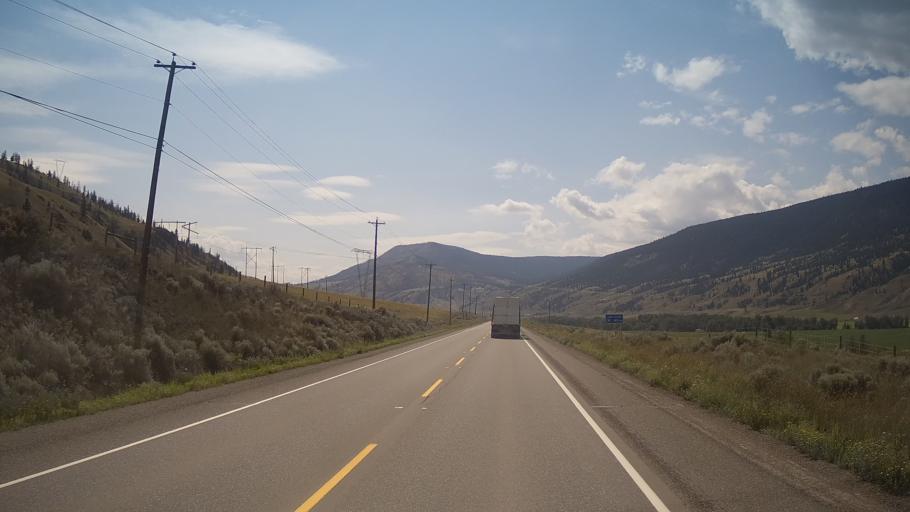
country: CA
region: British Columbia
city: Cache Creek
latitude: 50.8700
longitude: -121.3904
